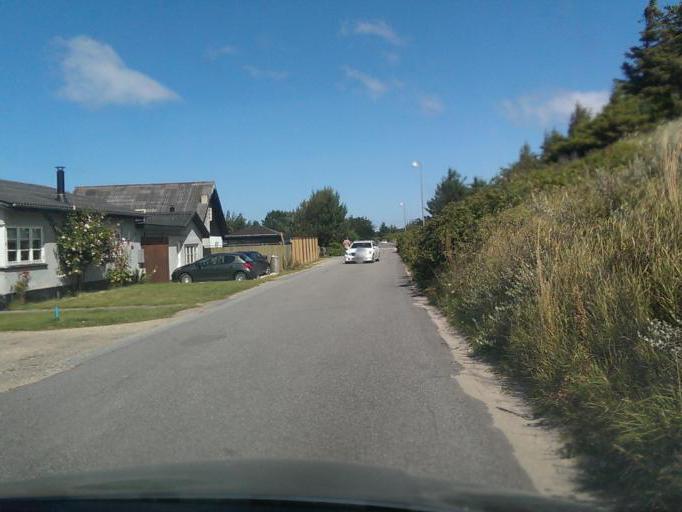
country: DK
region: North Denmark
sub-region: Jammerbugt Kommune
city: Pandrup
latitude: 57.2528
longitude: 9.5923
